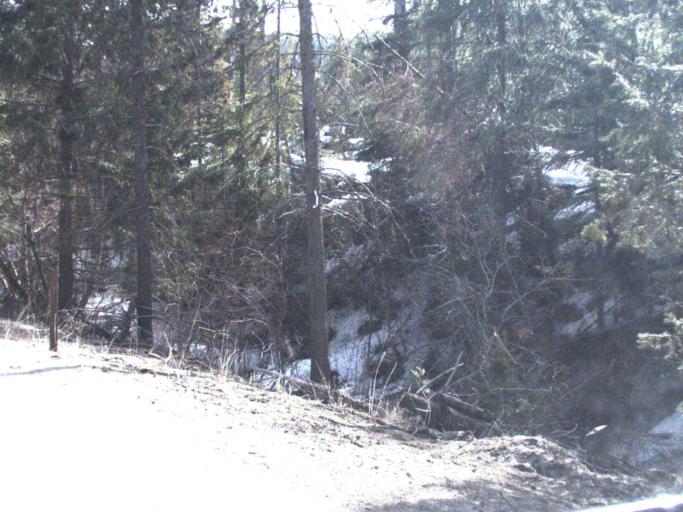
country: US
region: Washington
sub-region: Stevens County
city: Chewelah
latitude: 48.5310
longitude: -117.6207
